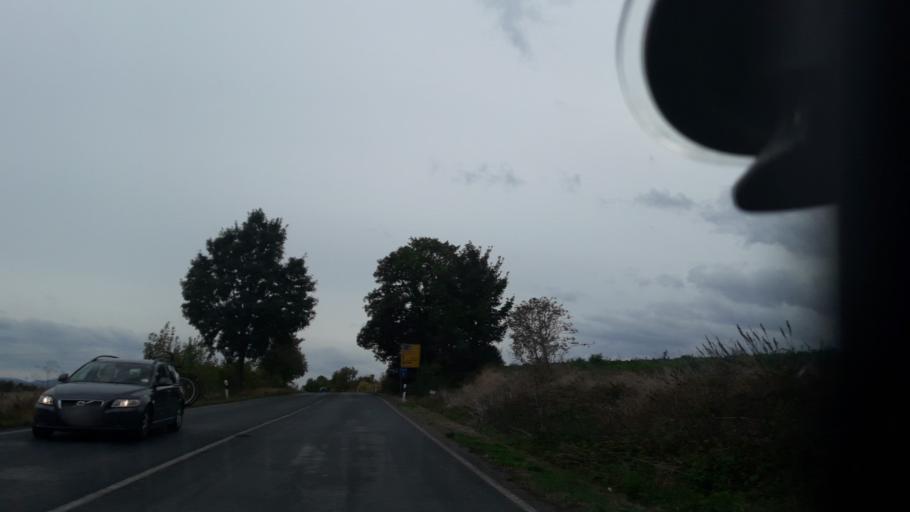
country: DE
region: Lower Saxony
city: Werlaburgdorf
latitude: 52.0555
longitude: 10.5447
